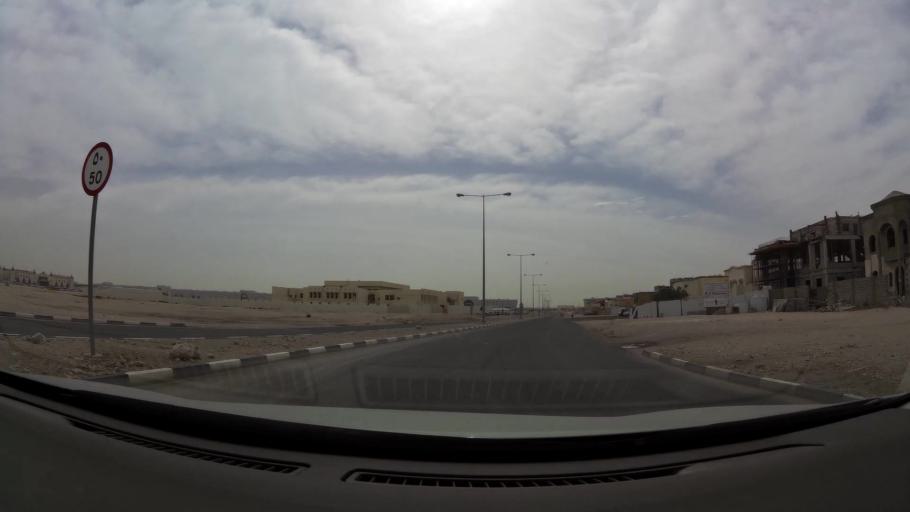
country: QA
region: Baladiyat ad Dawhah
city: Doha
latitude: 25.2165
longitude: 51.4911
